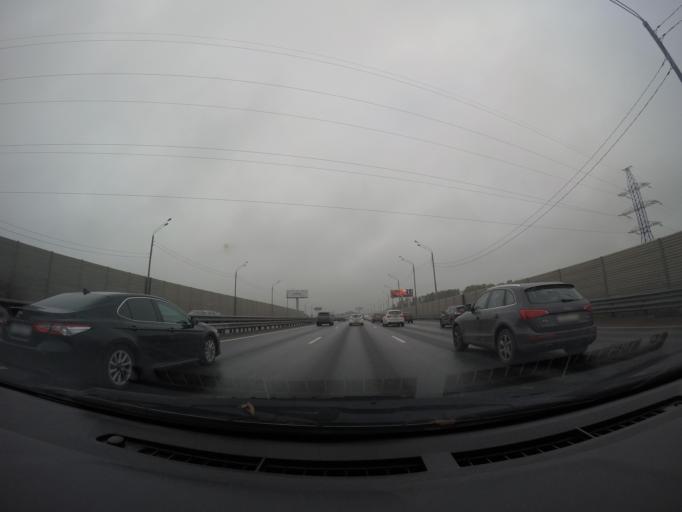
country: RU
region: Moskovskaya
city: Krasnogorsk
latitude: 55.8024
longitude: 37.3204
